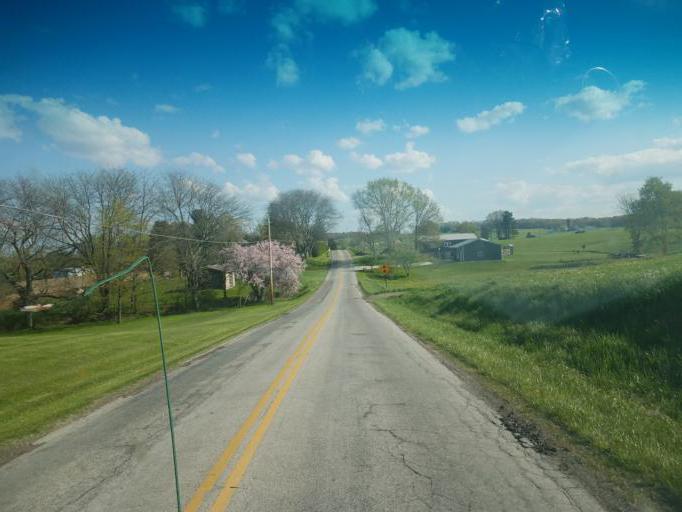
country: US
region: Ohio
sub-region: Wayne County
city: Apple Creek
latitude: 40.7603
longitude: -81.8775
